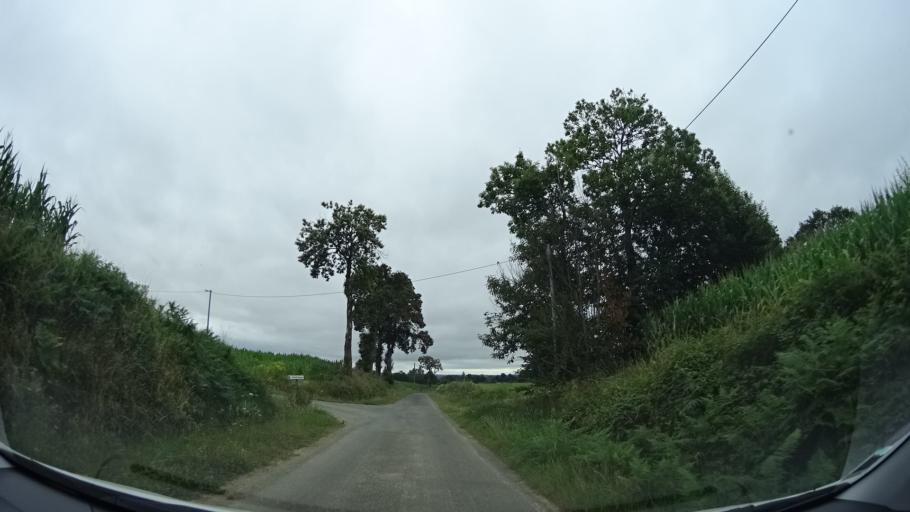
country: FR
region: Brittany
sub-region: Departement des Cotes-d'Armor
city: Evran
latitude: 48.3359
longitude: -1.9491
